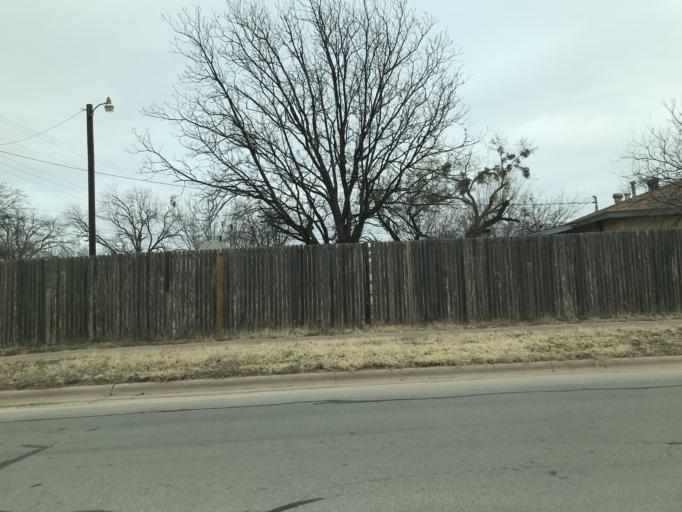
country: US
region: Texas
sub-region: Taylor County
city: Abilene
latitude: 32.4755
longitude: -99.7624
